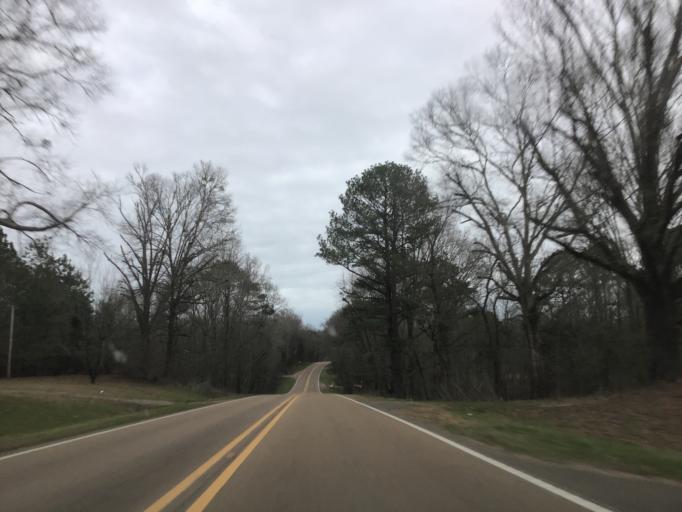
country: US
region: Mississippi
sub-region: Warren County
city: Beechwood
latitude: 32.2829
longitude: -90.7839
